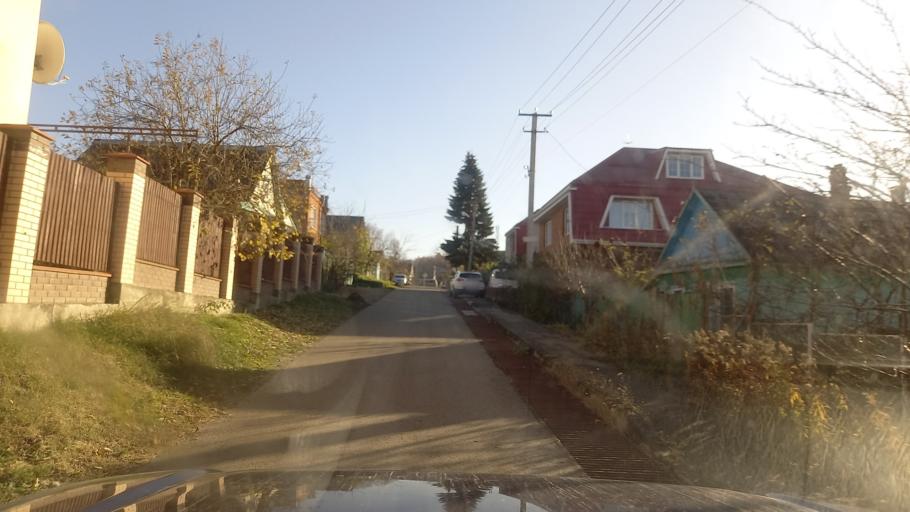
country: RU
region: Krasnodarskiy
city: Goryachiy Klyuch
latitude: 44.6207
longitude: 39.1040
